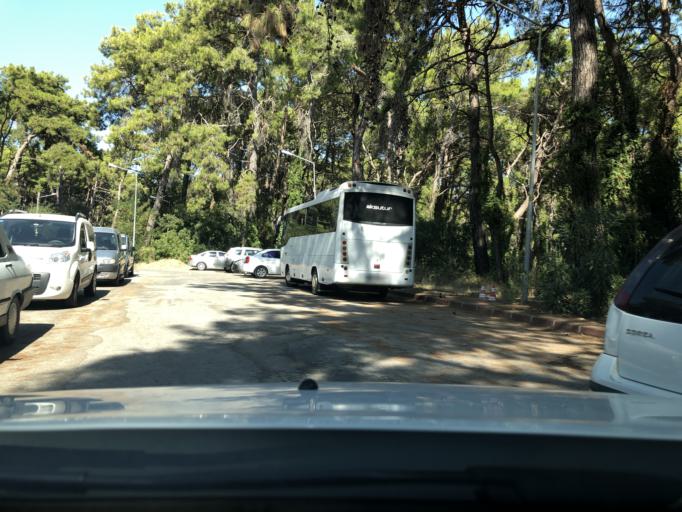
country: TR
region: Antalya
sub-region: Manavgat
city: Side
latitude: 36.7600
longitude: 31.4170
